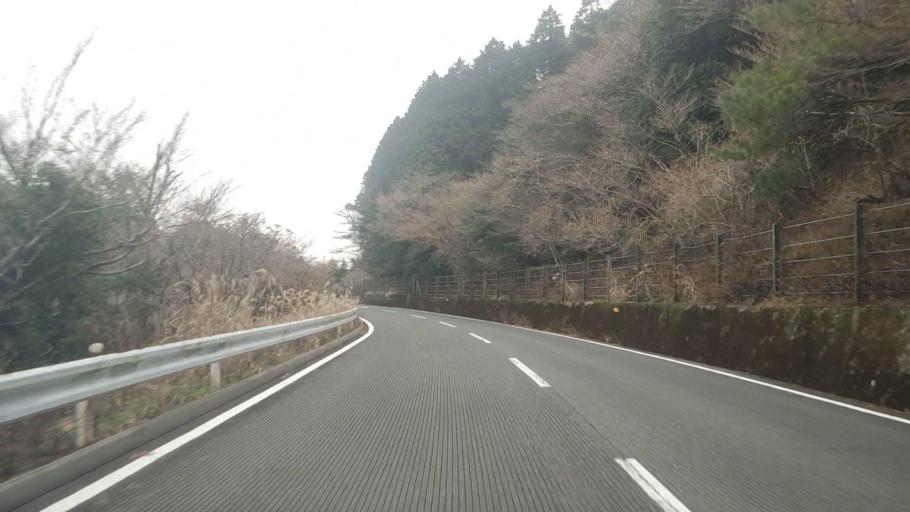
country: JP
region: Nagasaki
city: Shimabara
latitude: 32.7686
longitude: 130.2718
